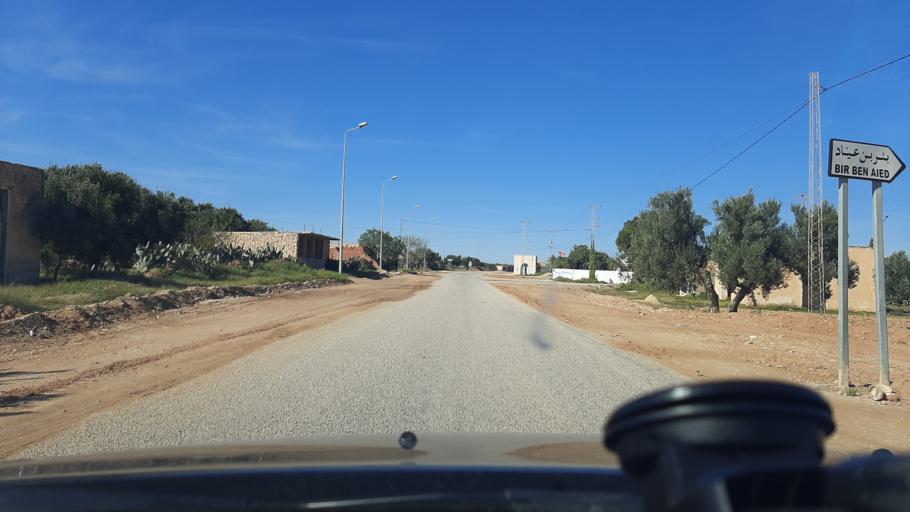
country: TN
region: Safaqis
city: Sfax
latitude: 34.9089
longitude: 10.5933
